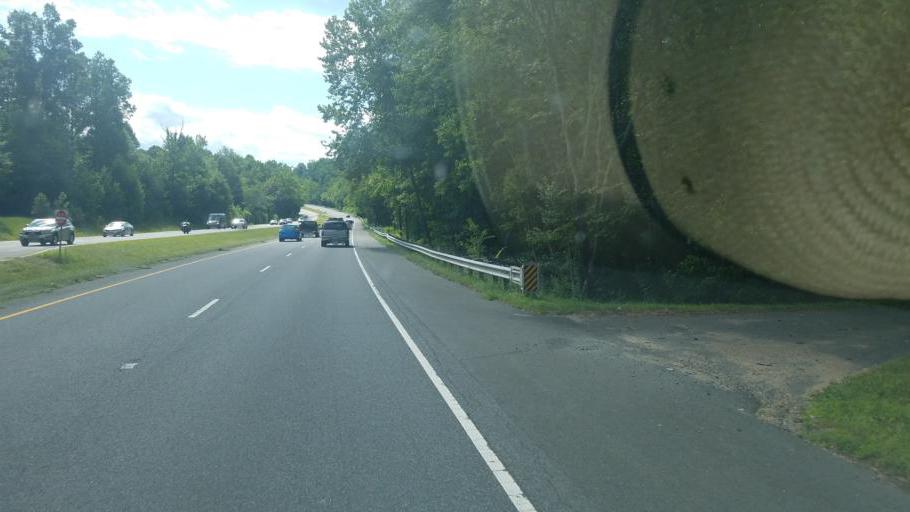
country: US
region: Virginia
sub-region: Stafford County
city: Falmouth
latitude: 38.4151
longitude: -77.6075
